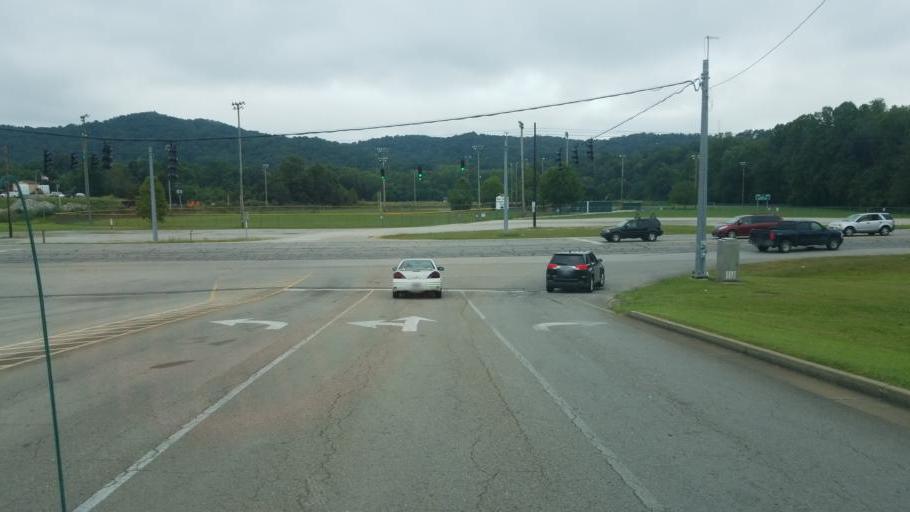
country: US
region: Kentucky
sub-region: Rowan County
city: Morehead
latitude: 38.1998
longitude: -83.4796
